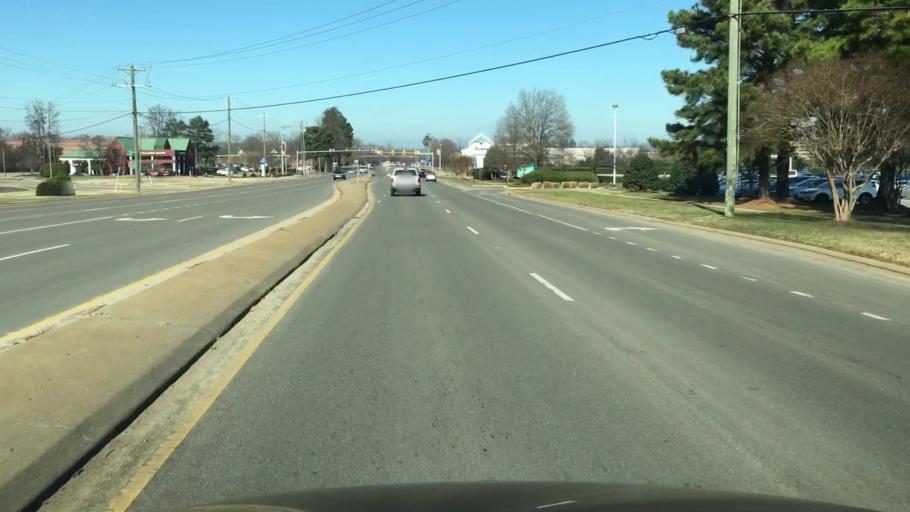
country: US
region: Virginia
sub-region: Chesterfield County
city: Bon Air
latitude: 37.5060
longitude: -77.6119
